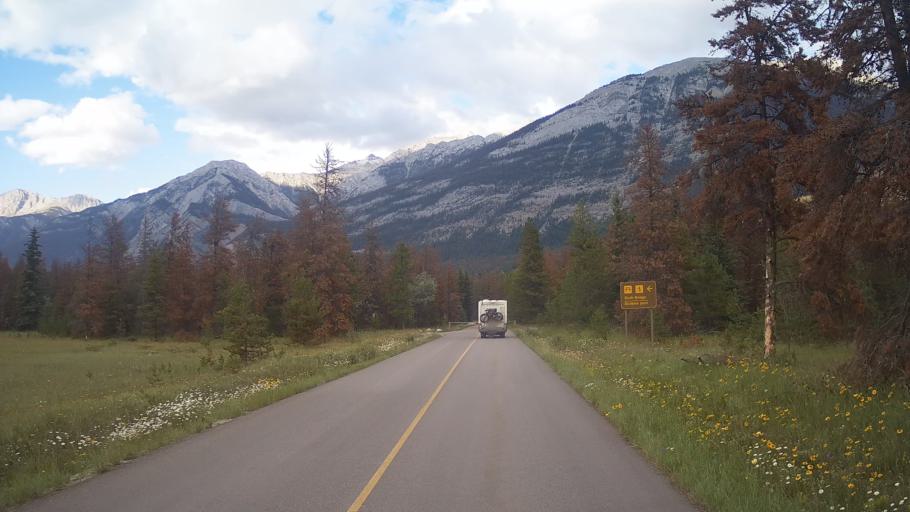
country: CA
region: Alberta
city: Jasper Park Lodge
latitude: 52.9279
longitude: -118.0304
